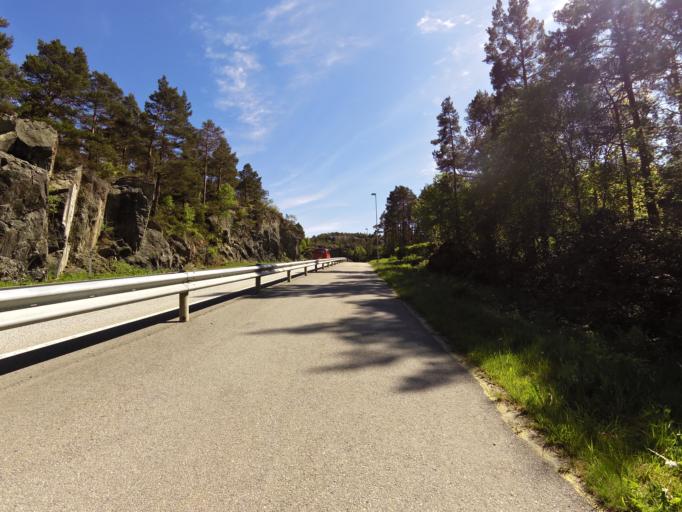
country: NO
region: Hordaland
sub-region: Stord
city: Sagvag
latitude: 59.7855
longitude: 5.3741
